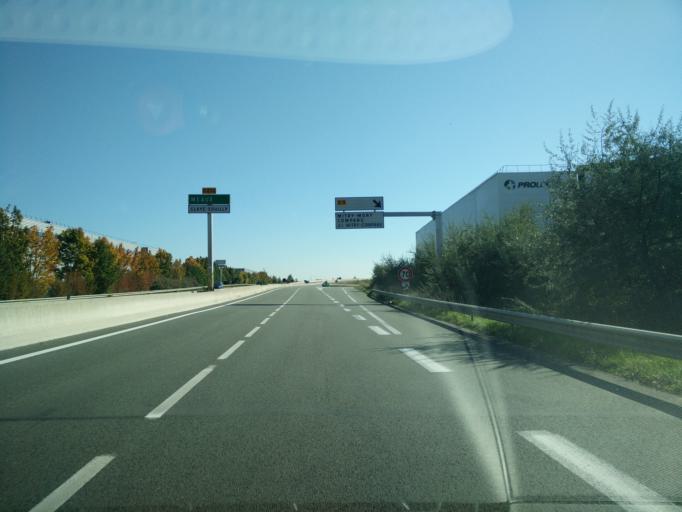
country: FR
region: Ile-de-France
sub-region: Departement de Seine-et-Marne
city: Mitry-Mory
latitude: 48.9947
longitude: 2.6507
